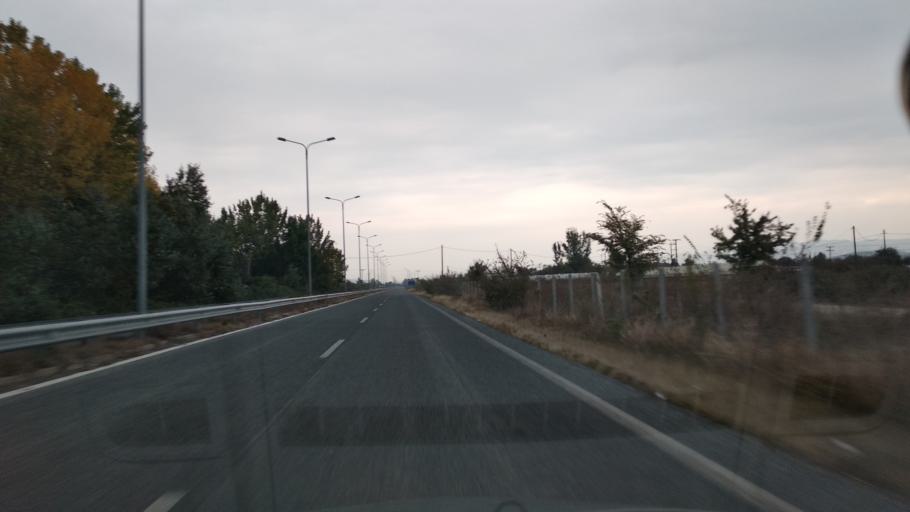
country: GR
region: Thessaly
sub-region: Trikala
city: Pyrgetos
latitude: 39.5451
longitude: 21.7352
